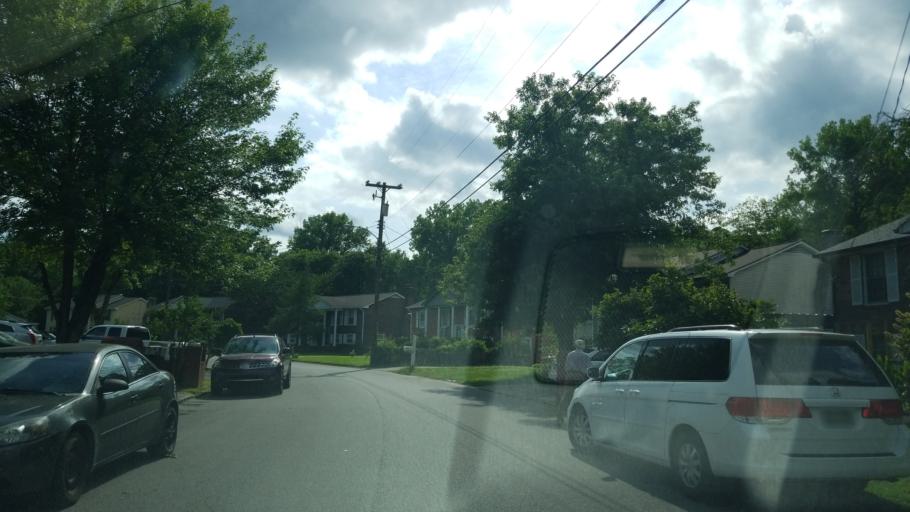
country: US
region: Tennessee
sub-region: Williamson County
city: Brentwood Estates
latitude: 36.0533
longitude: -86.6816
